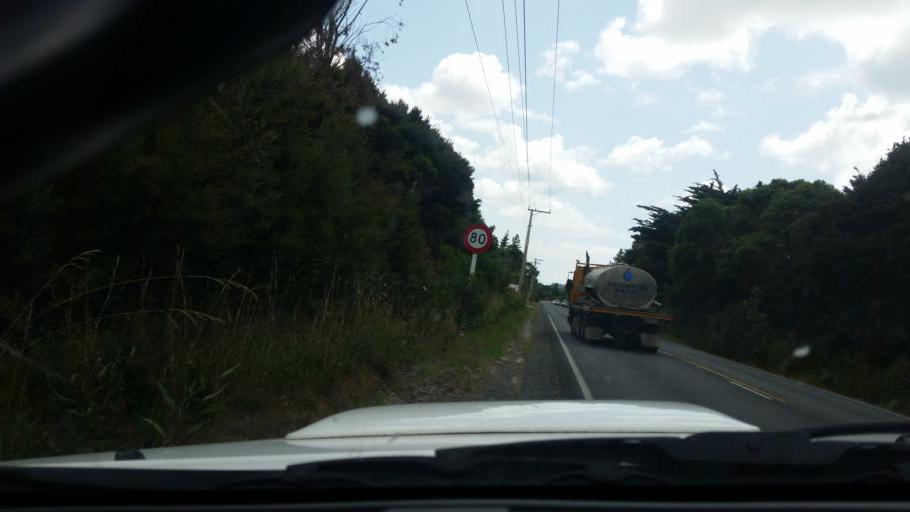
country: NZ
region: Auckland
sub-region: Auckland
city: Wellsford
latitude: -36.1211
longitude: 174.5722
